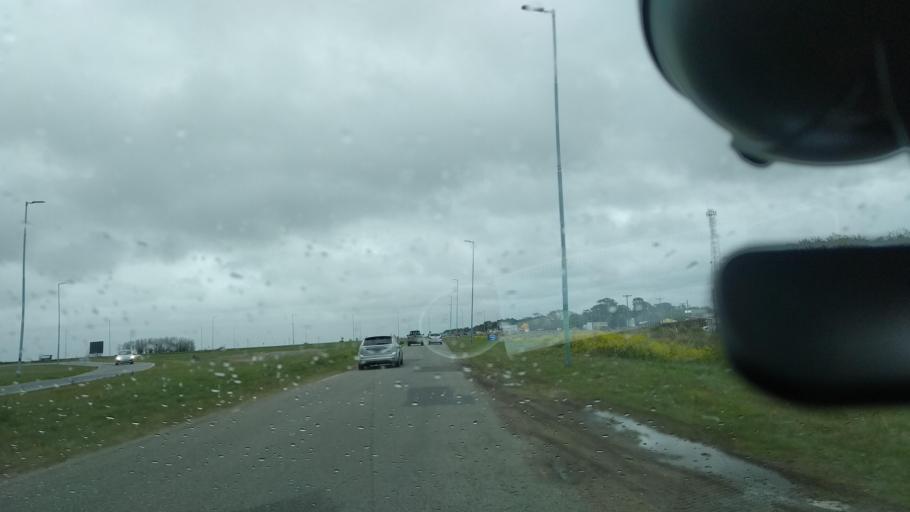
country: AR
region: Buenos Aires
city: San Clemente del Tuyu
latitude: -36.3882
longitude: -56.7375
